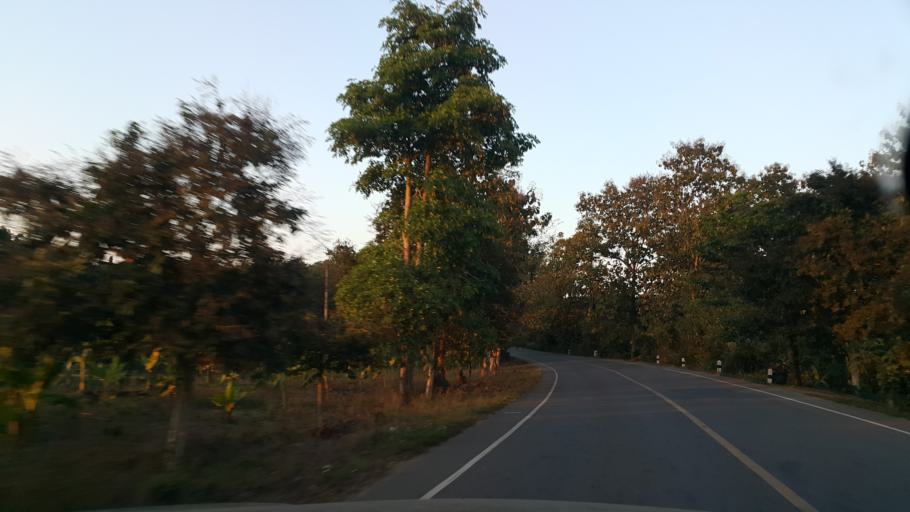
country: TH
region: Phrae
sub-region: Amphoe Wang Chin
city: Wang Chin
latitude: 17.8517
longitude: 99.6277
